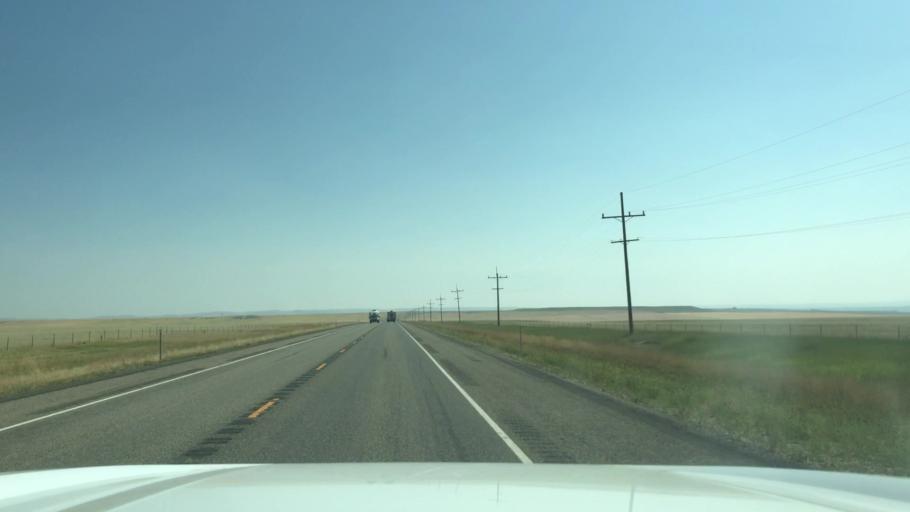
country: US
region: Montana
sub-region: Wheatland County
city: Harlowton
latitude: 46.5025
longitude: -109.7663
